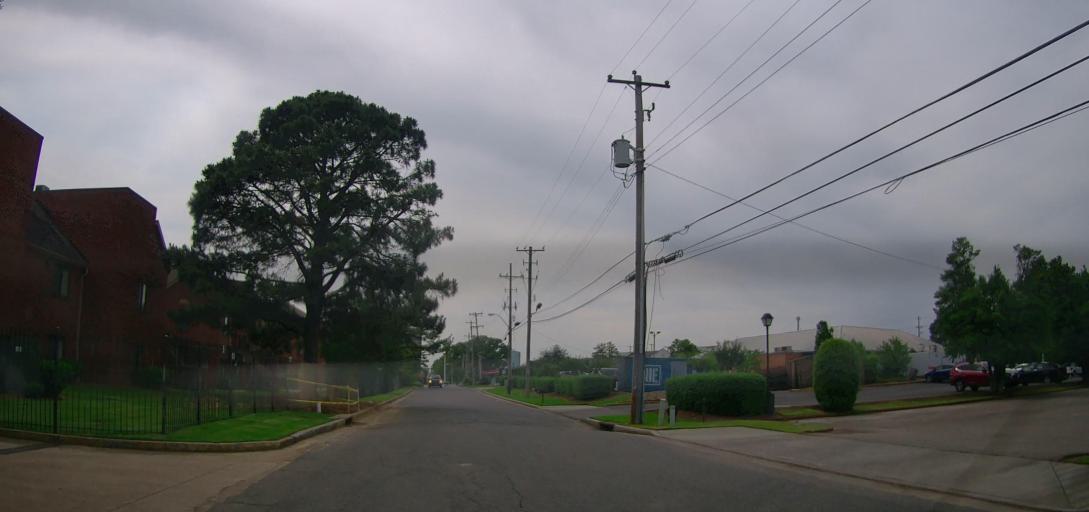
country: US
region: Tennessee
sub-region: Shelby County
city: Germantown
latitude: 35.1006
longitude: -89.8565
